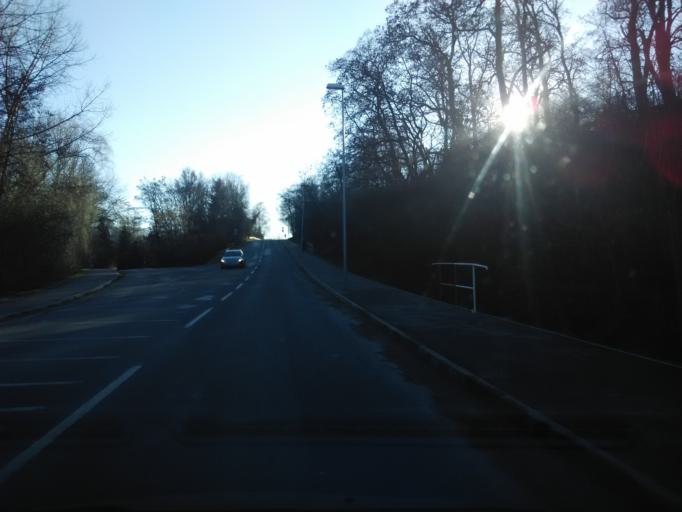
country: SK
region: Zilinsky
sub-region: Okres Zilina
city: Zilina
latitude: 49.2126
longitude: 18.7728
